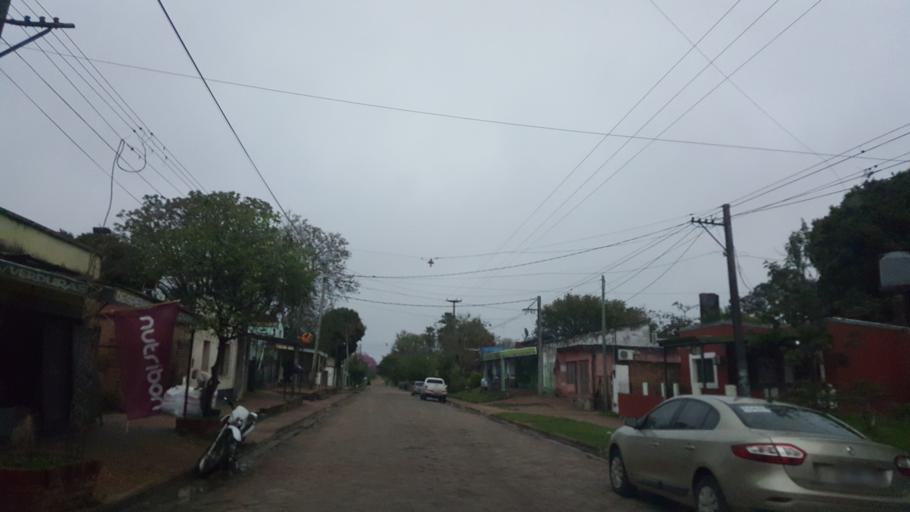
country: AR
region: Corrientes
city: Ituzaingo
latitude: -27.5894
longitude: -56.6926
